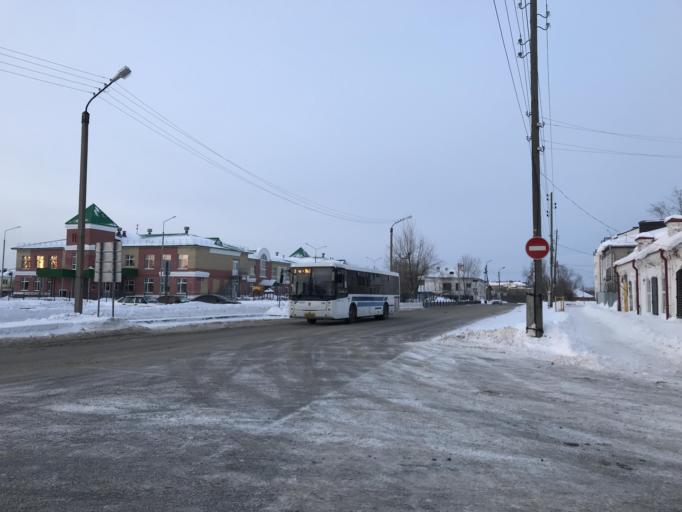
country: RU
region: Tjumen
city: Tobol'sk
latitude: 58.1935
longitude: 68.2415
